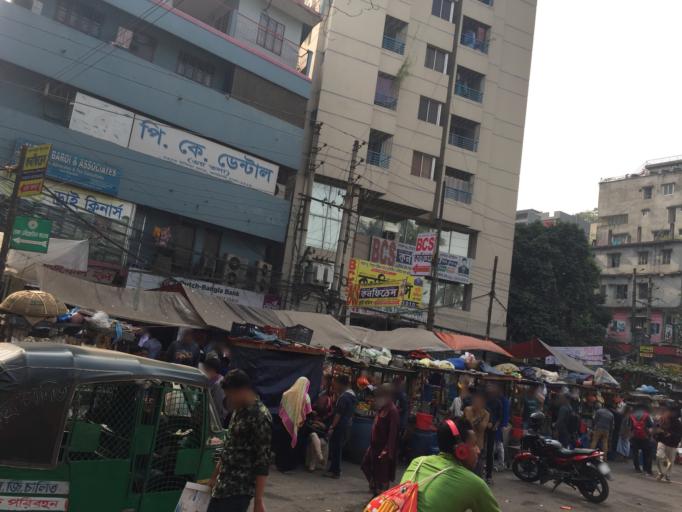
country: BD
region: Dhaka
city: Azimpur
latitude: 23.7583
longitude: 90.3874
